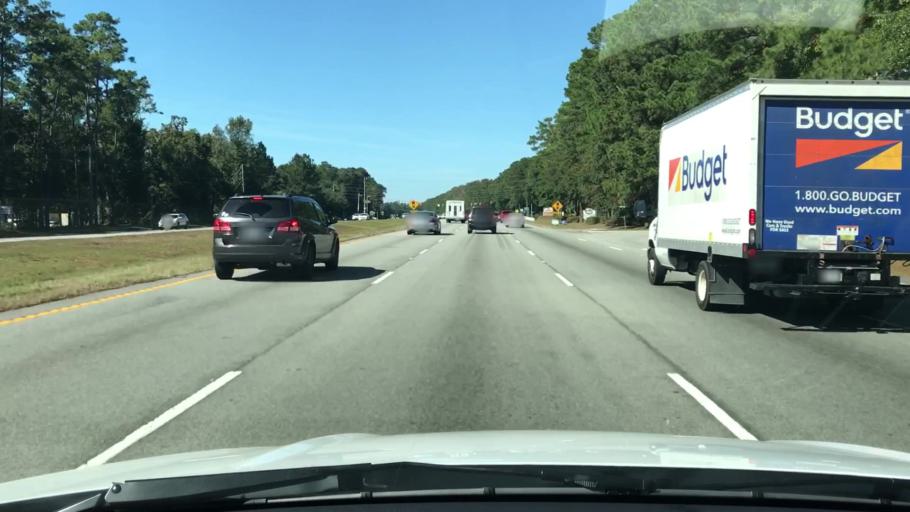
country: US
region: South Carolina
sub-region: Beaufort County
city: Bluffton
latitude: 32.2659
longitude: -80.8584
